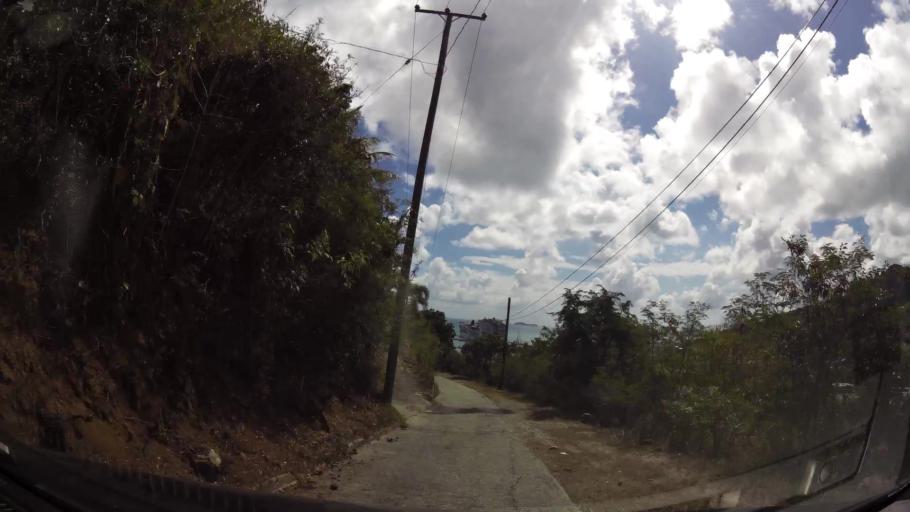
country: VG
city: Road Town
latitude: 18.4293
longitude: -64.6205
